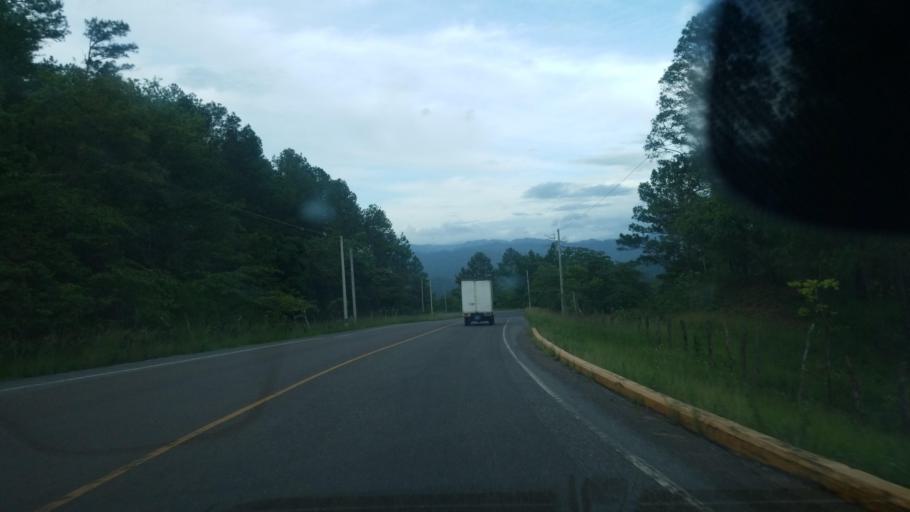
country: HN
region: Santa Barbara
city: Concepcion del Sur
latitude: 14.7966
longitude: -88.1591
